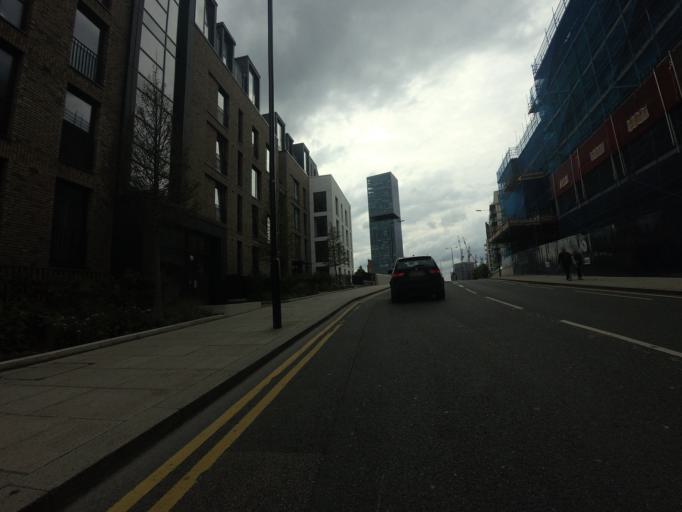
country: GB
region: England
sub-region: Greater London
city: Poplar
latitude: 51.5461
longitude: -0.0027
